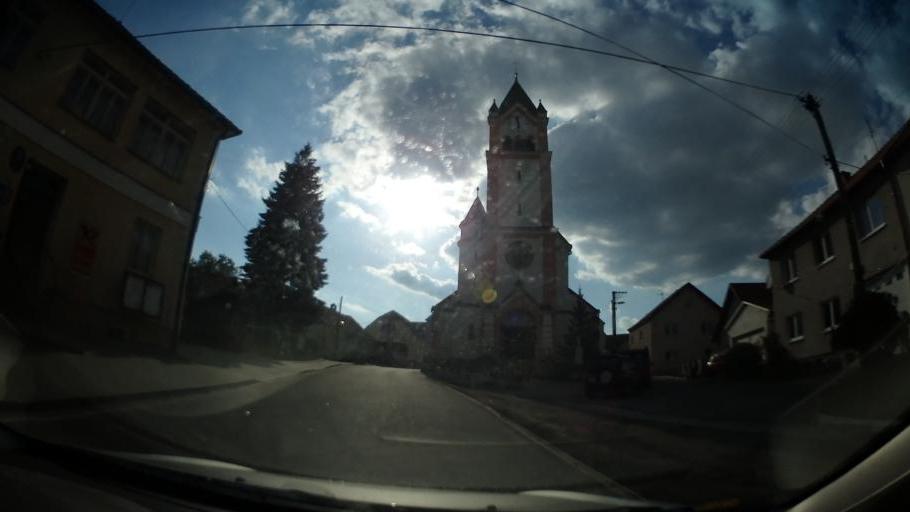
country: CZ
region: Vysocina
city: Merin
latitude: 49.3499
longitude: 15.9383
